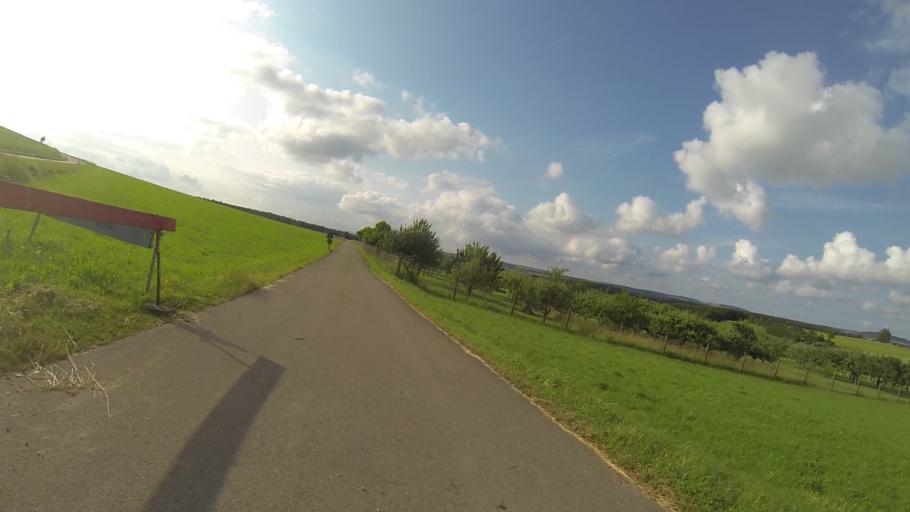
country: DE
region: Baden-Wuerttemberg
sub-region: Regierungsbezirk Stuttgart
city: Neresheim
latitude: 48.7319
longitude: 10.2884
